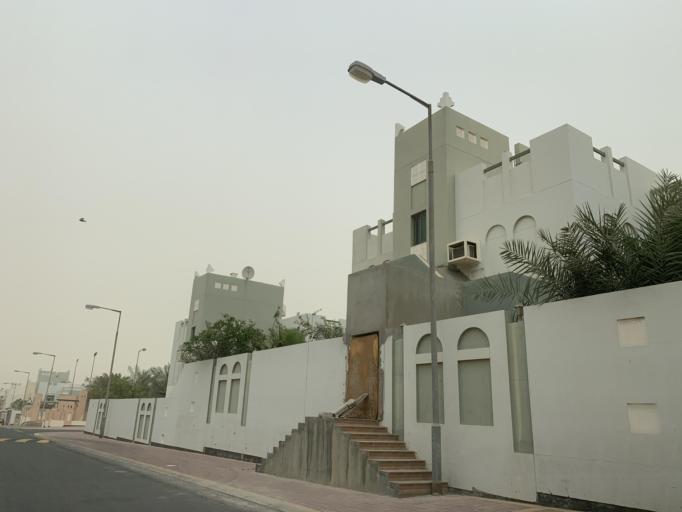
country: BH
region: Central Governorate
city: Madinat Hamad
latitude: 26.1277
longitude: 50.5097
